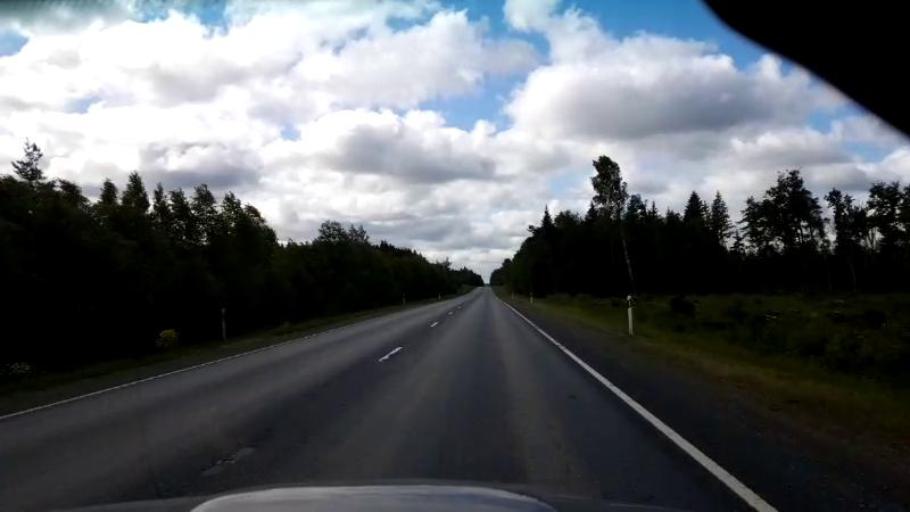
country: EE
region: Harju
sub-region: Saue linn
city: Saue
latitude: 59.1875
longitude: 24.5002
